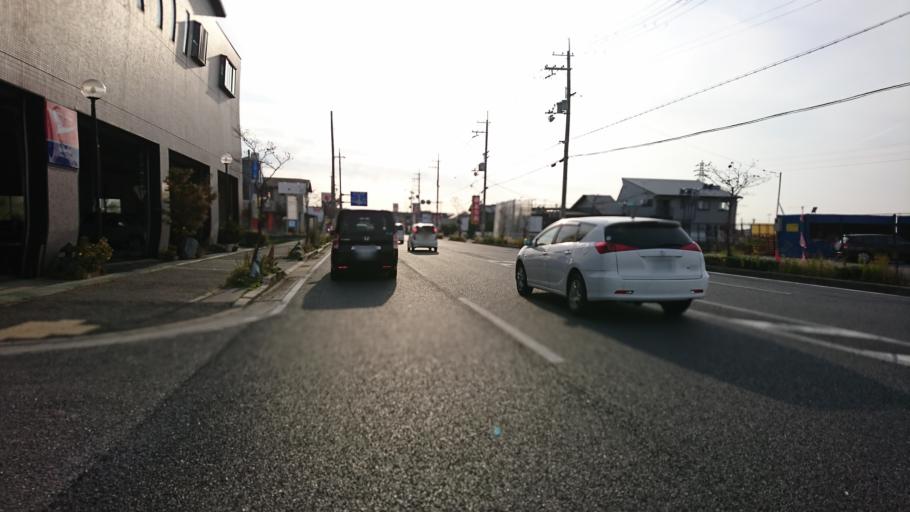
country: JP
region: Hyogo
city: Kakogawacho-honmachi
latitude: 34.7117
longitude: 134.8837
